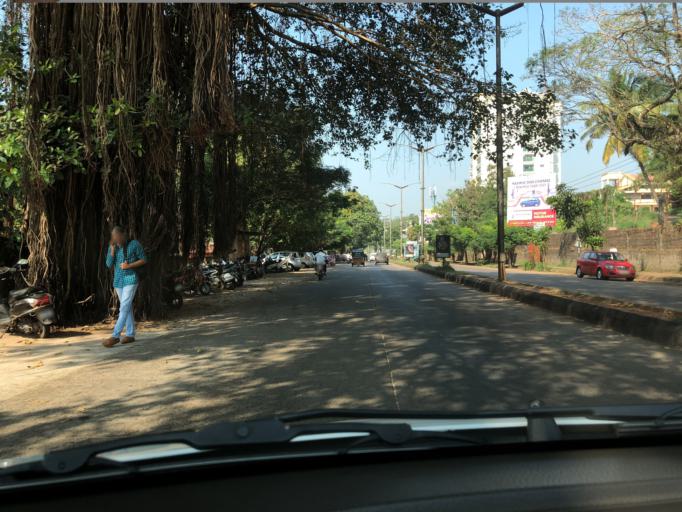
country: IN
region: Karnataka
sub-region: Dakshina Kannada
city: Mangalore
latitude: 12.8893
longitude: 74.8351
